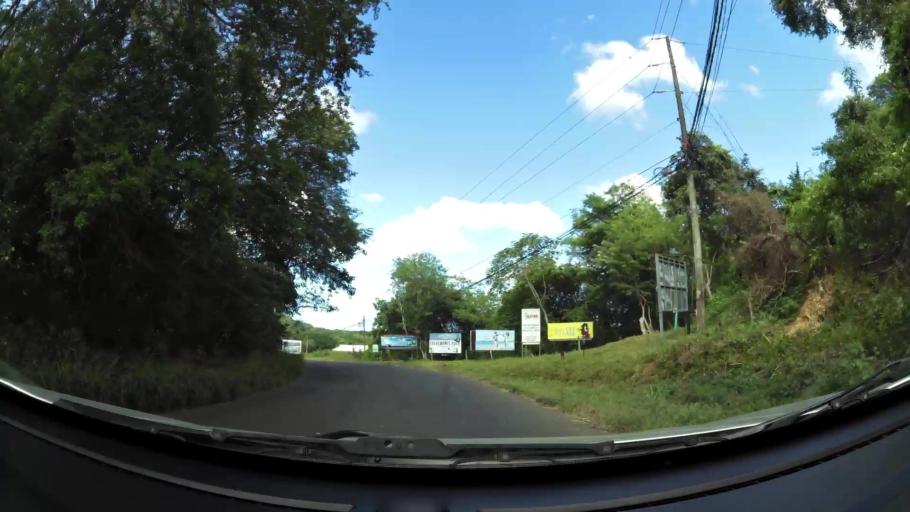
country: CR
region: Guanacaste
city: Santa Cruz
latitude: 10.3097
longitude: -85.8123
